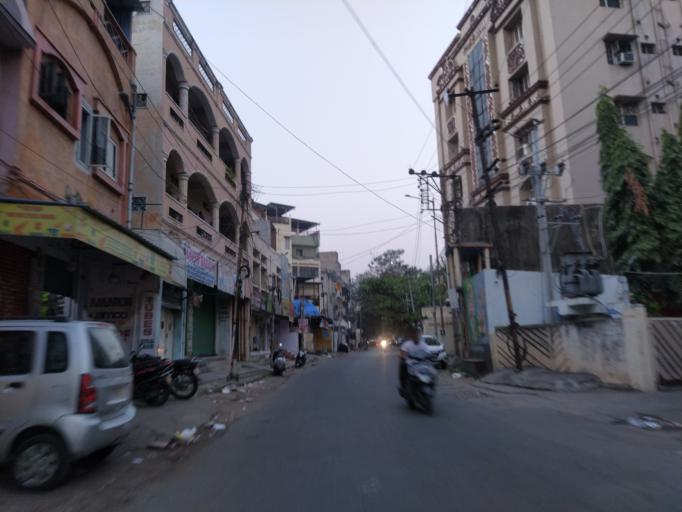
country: IN
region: Telangana
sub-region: Hyderabad
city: Hyderabad
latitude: 17.3909
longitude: 78.4857
